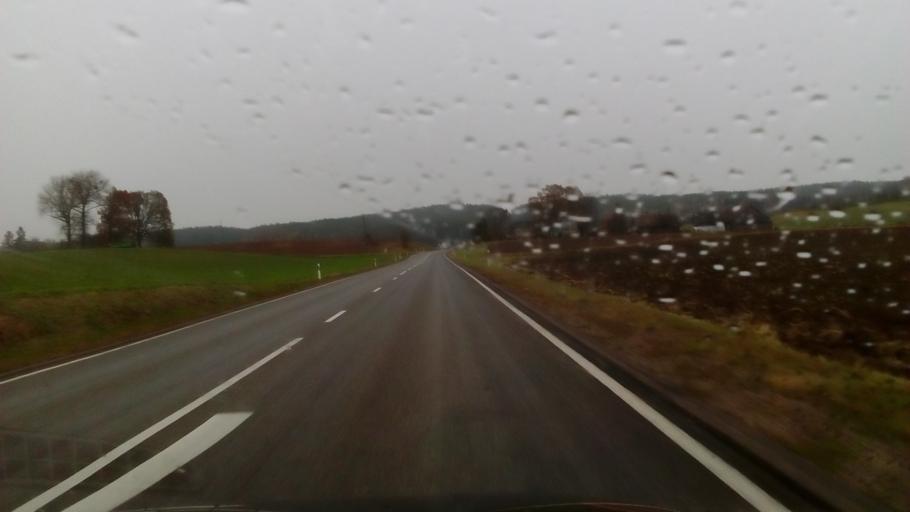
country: LT
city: Prienai
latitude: 54.5937
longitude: 23.8376
